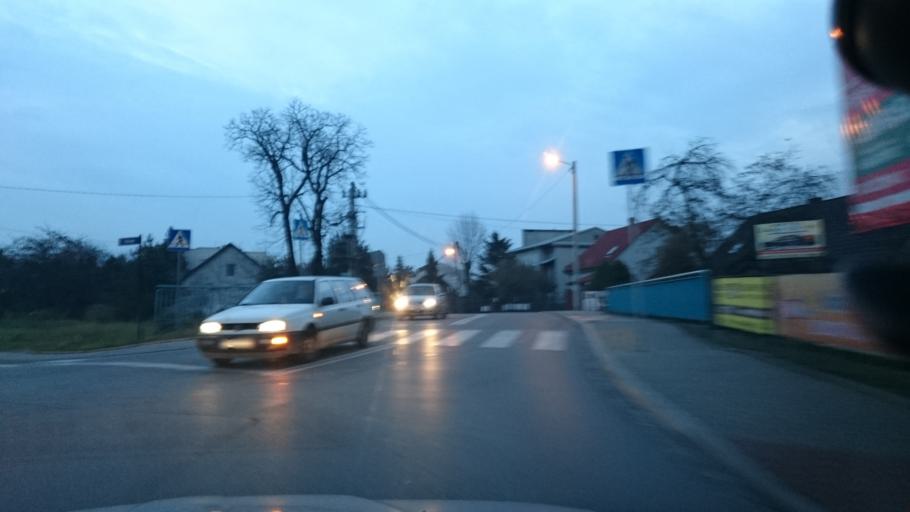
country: PL
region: Lesser Poland Voivodeship
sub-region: Powiat wielicki
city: Czarnochowice
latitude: 50.0185
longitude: 20.0357
